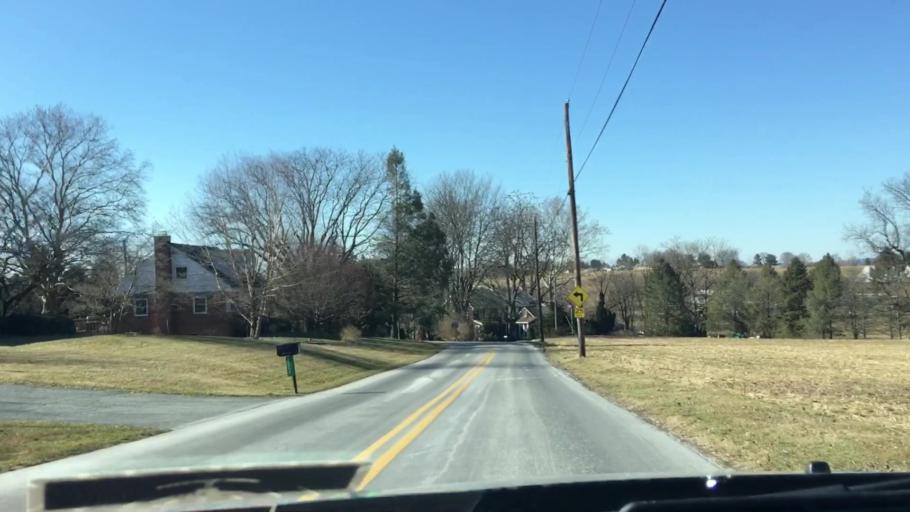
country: US
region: Pennsylvania
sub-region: Lancaster County
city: Brownstown
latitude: 40.0682
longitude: -76.2273
